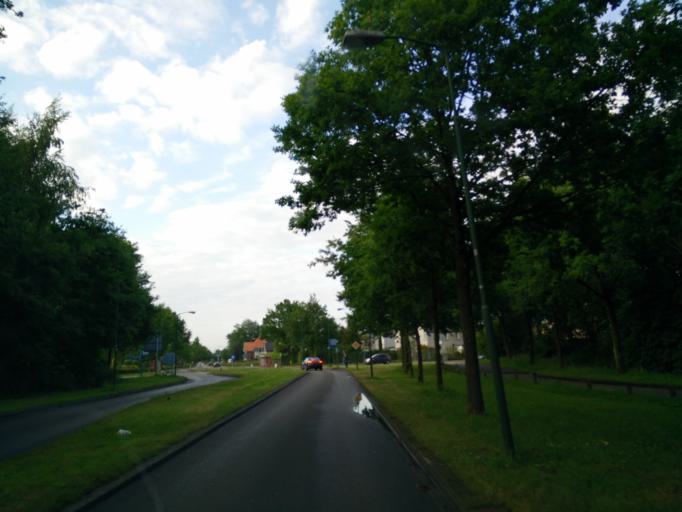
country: NL
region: Utrecht
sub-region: Gemeente Woudenberg
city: Woudenberg
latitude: 52.0779
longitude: 5.4123
